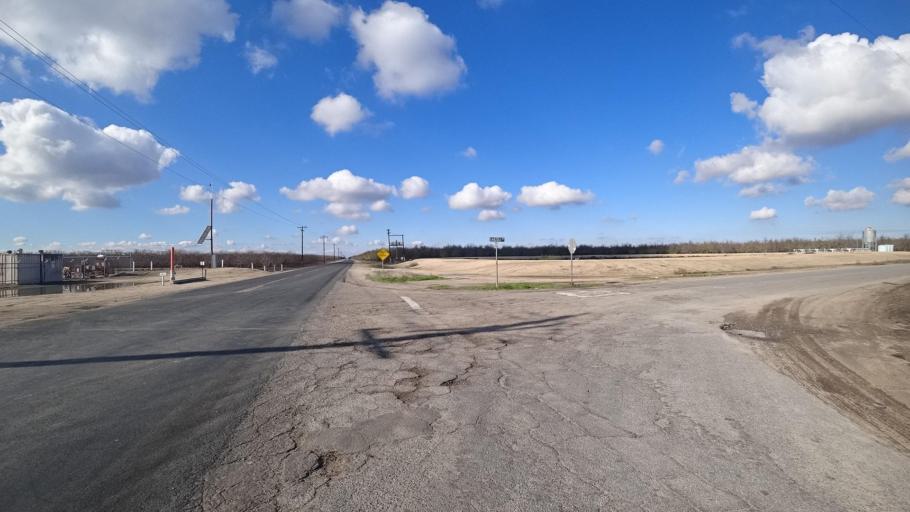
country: US
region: California
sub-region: Kern County
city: McFarland
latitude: 35.6454
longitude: -119.2409
